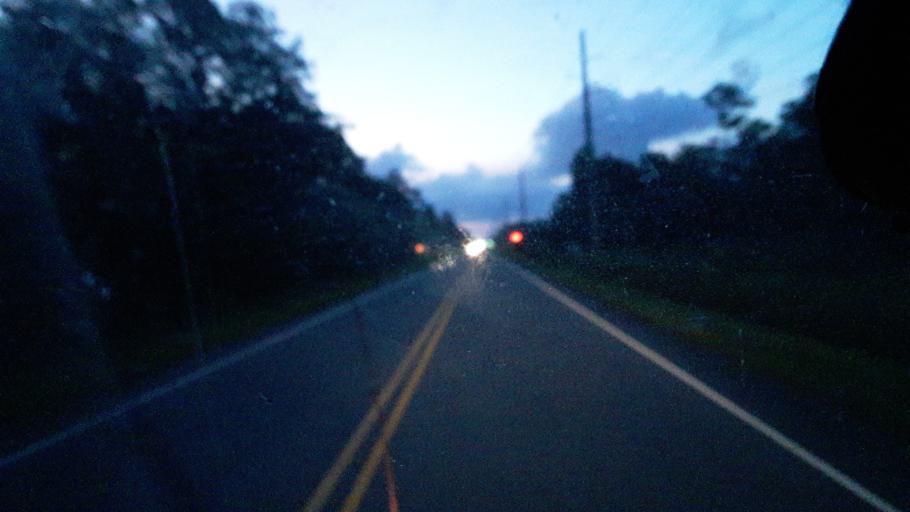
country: US
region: North Carolina
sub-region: Brunswick County
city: Oak Island
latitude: 33.9914
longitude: -78.2115
